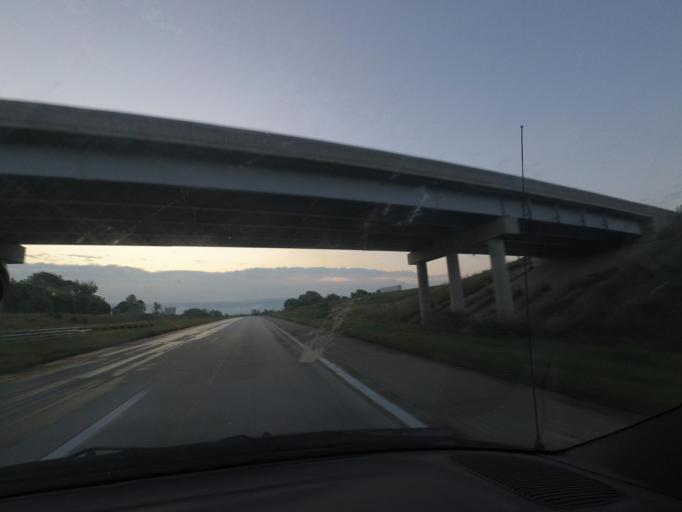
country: US
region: Missouri
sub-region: Macon County
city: Macon
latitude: 39.7550
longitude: -92.6254
